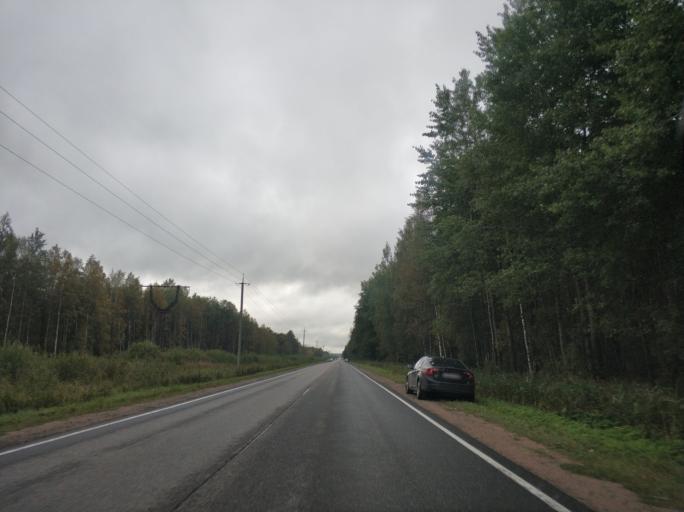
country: RU
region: Leningrad
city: Borisova Griva
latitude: 60.1112
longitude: 30.9617
